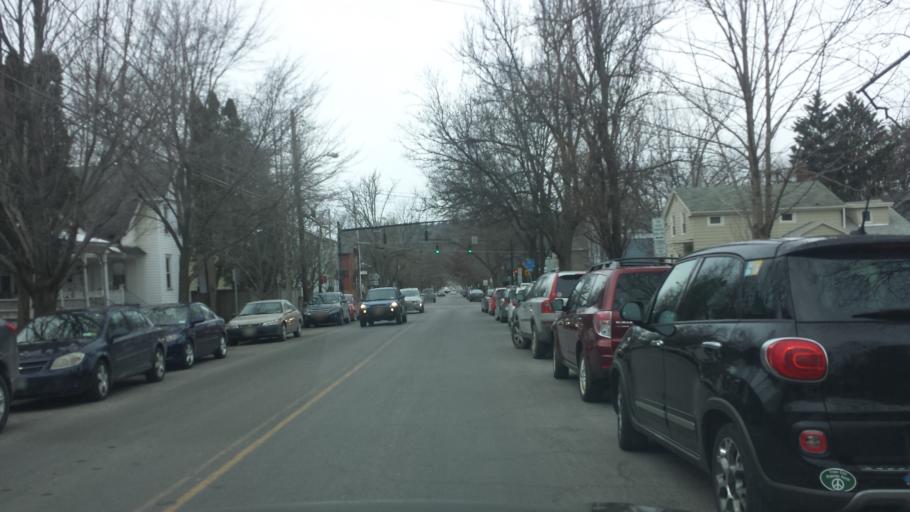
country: US
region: New York
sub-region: Tompkins County
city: Ithaca
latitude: 42.4413
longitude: -76.5031
